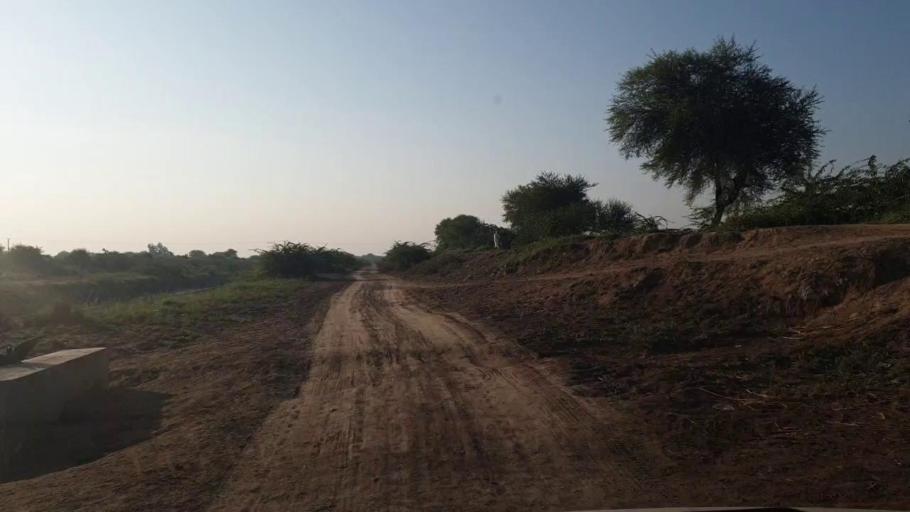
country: PK
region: Sindh
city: Badin
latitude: 24.6336
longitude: 68.7947
